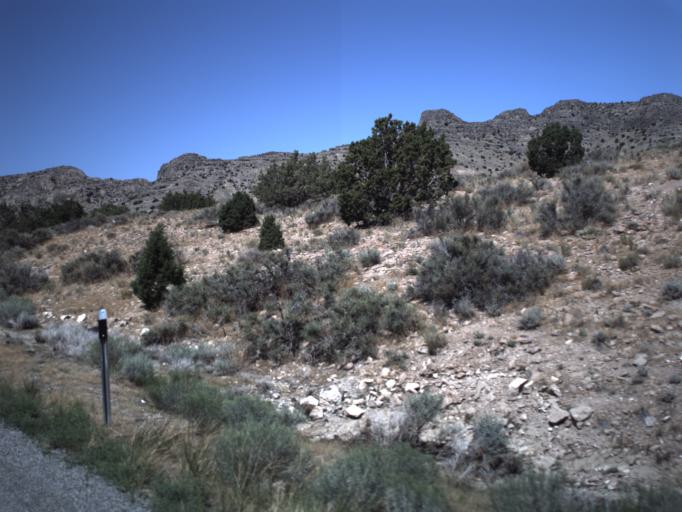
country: US
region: Utah
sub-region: Beaver County
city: Milford
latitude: 39.0747
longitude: -113.6364
